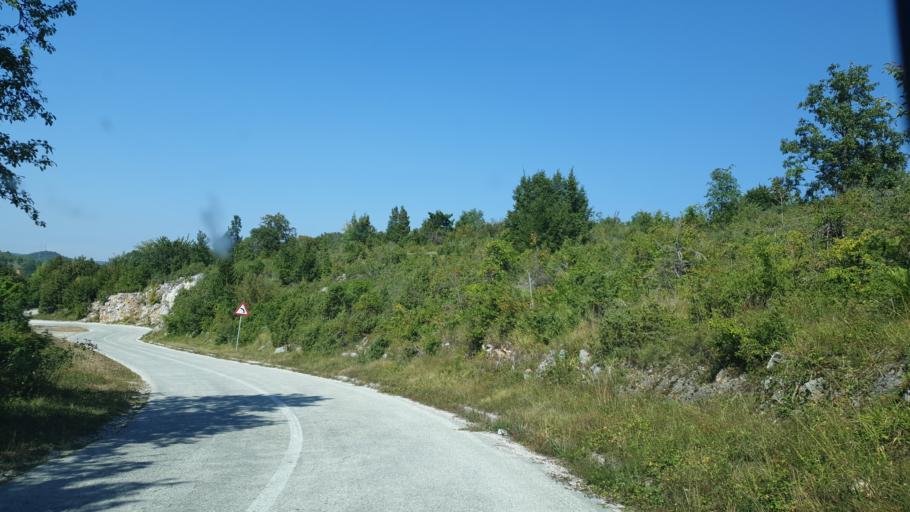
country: RS
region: Central Serbia
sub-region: Zlatiborski Okrug
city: Cajetina
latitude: 43.6816
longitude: 19.8517
